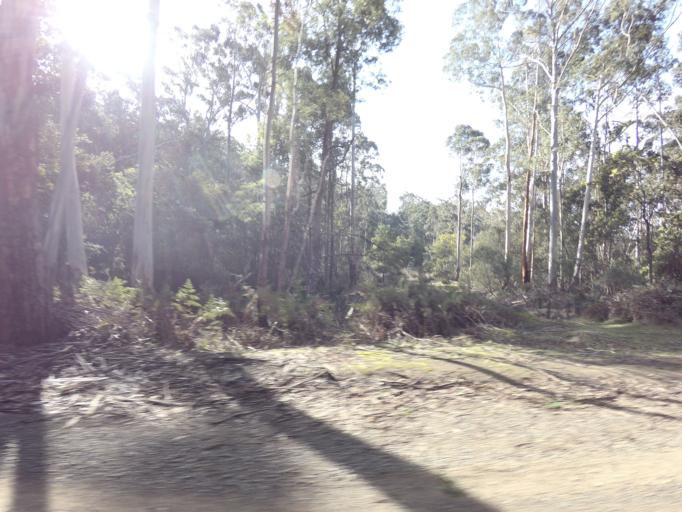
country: AU
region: Tasmania
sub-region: Kingborough
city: Kettering
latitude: -43.1074
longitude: 147.2569
